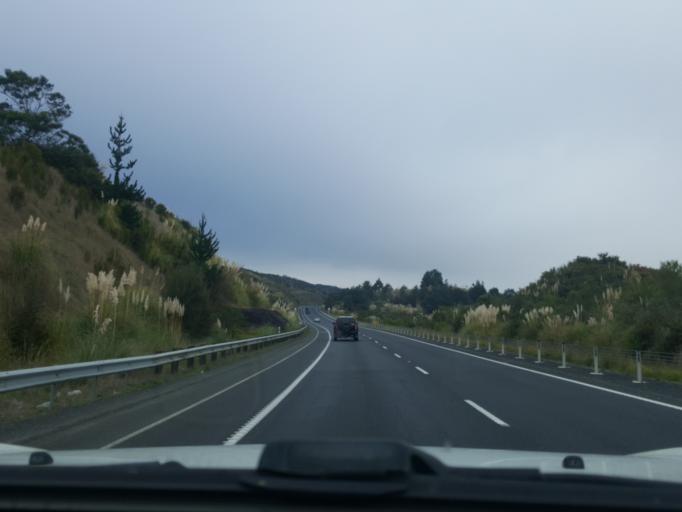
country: NZ
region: Auckland
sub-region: Auckland
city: Pukekohe East
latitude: -37.2853
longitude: 175.0527
